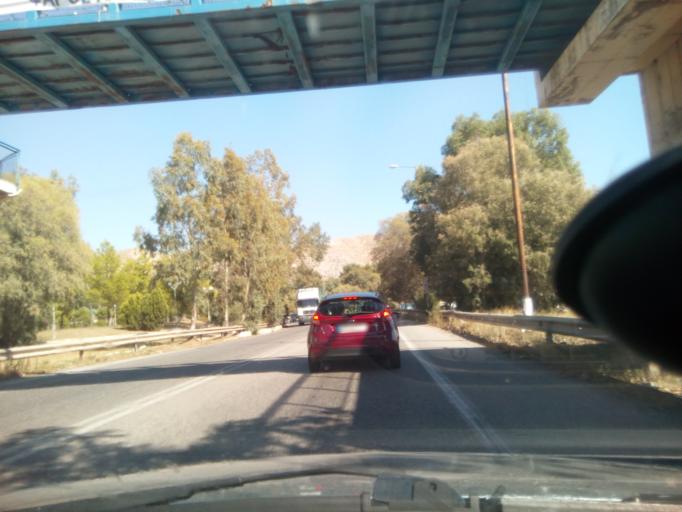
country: GR
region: Central Greece
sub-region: Nomos Evvoias
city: Chalkida
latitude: 38.4553
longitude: 23.6079
